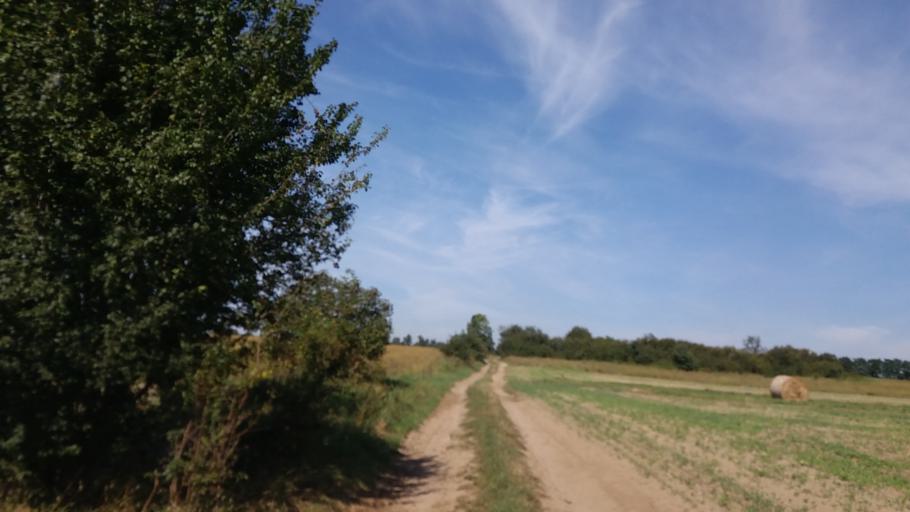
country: PL
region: West Pomeranian Voivodeship
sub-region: Powiat choszczenski
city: Choszczno
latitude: 53.1172
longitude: 15.4130
